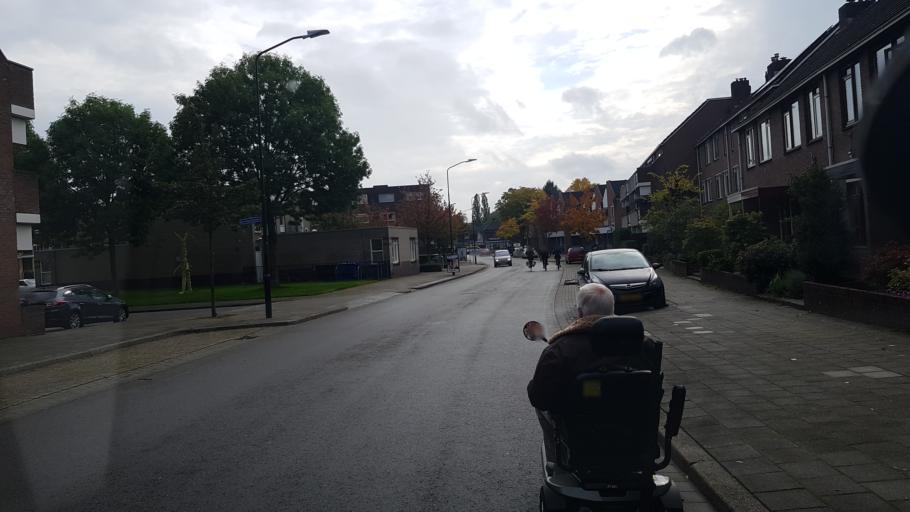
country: NL
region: Gelderland
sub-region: Gemeente Apeldoorn
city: Apeldoorn
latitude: 52.2014
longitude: 5.9550
